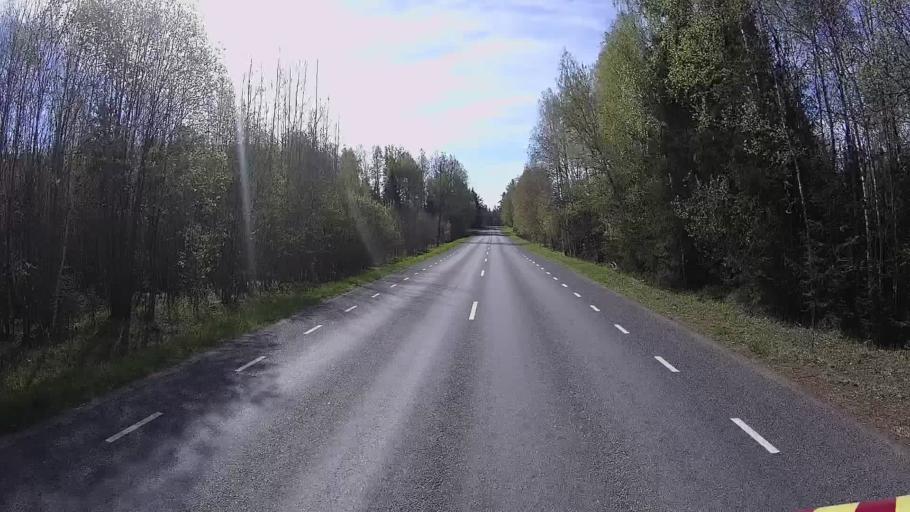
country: EE
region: Polvamaa
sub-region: Polva linn
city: Polva
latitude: 58.1782
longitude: 27.1127
